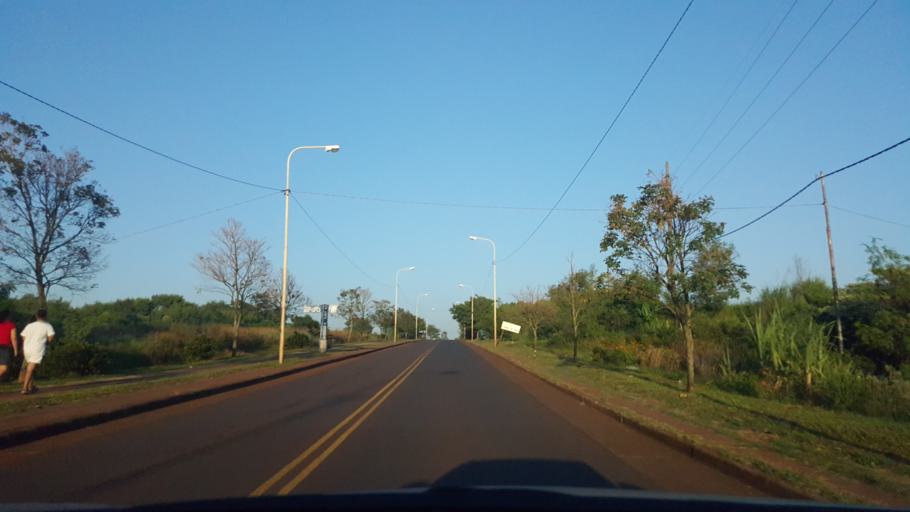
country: AR
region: Misiones
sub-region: Departamento de Capital
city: Posadas
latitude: -27.3727
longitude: -55.9578
